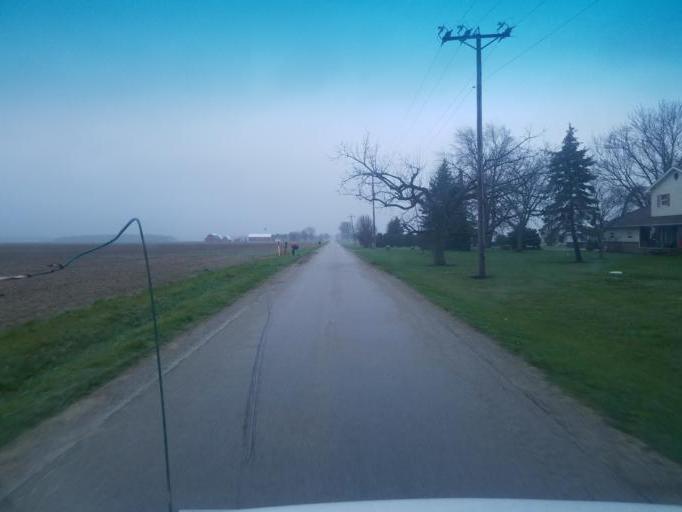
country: US
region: Ohio
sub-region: Fulton County
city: Archbold
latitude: 41.4273
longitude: -84.2479
